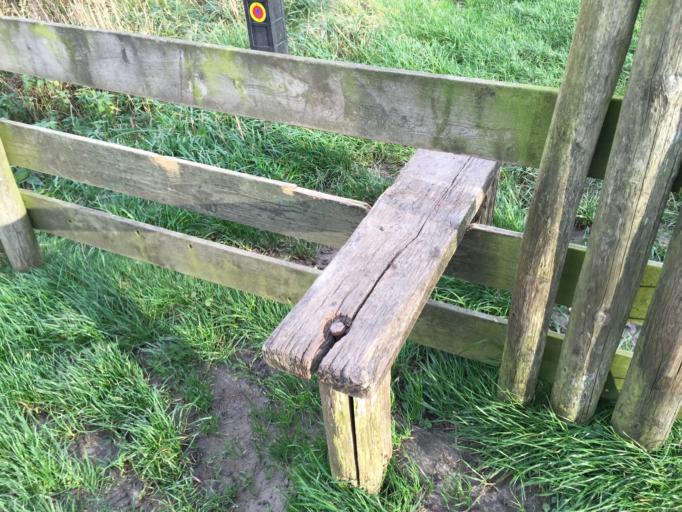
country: NL
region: North Holland
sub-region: Gemeente Ouder-Amstel
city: Ouderkerk aan de Amstel
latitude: 52.2490
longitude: 4.9151
